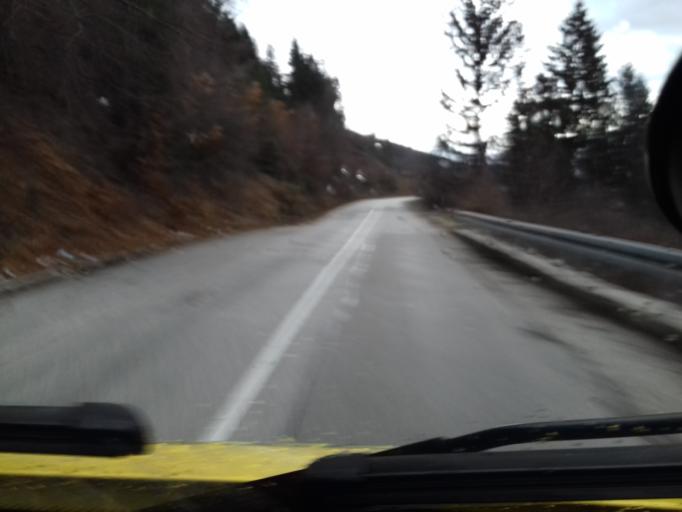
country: BA
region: Federation of Bosnia and Herzegovina
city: Turbe
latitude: 44.2724
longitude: 17.5150
